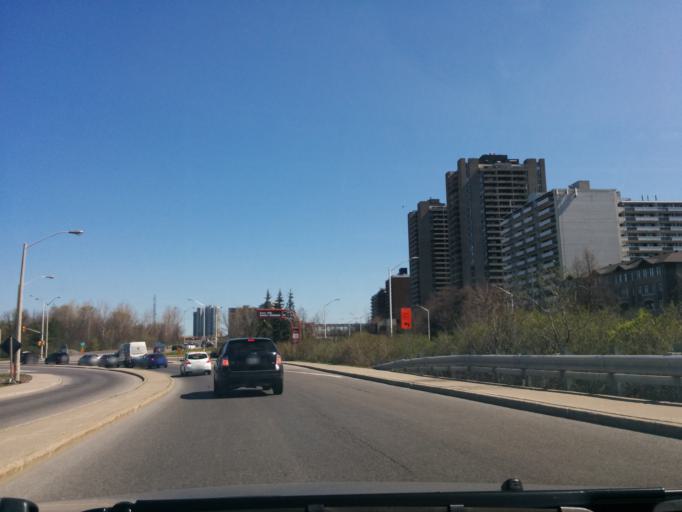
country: CA
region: Ontario
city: Ottawa
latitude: 45.3996
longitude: -75.6680
